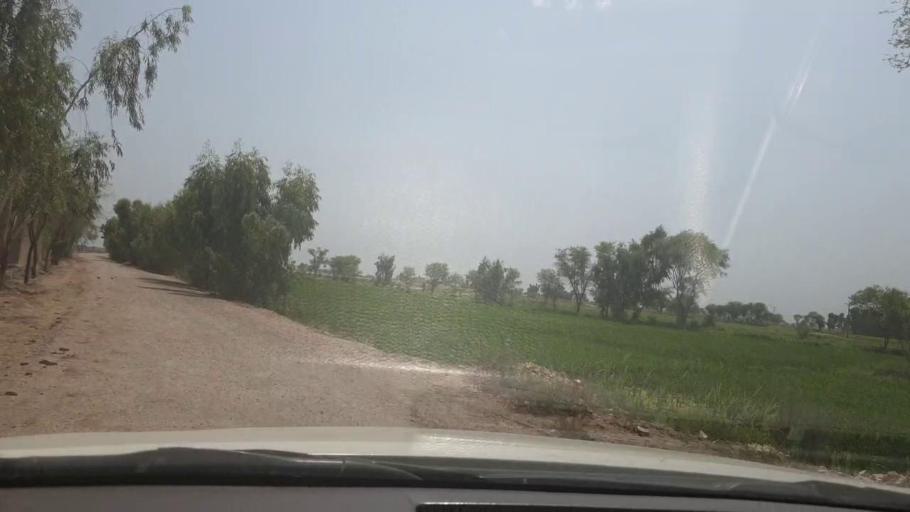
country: PK
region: Sindh
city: Shikarpur
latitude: 28.0395
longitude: 68.5735
